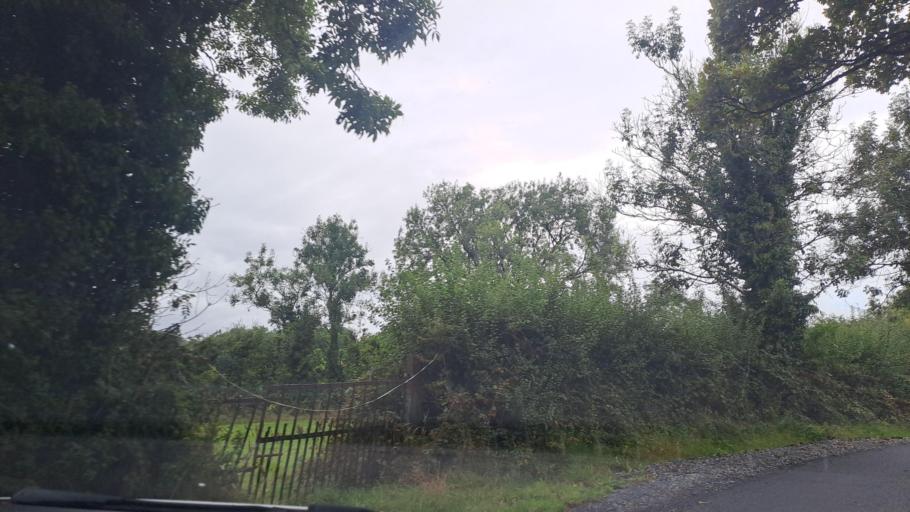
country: IE
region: Ulster
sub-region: An Cabhan
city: Kingscourt
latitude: 53.9801
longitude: -6.8141
